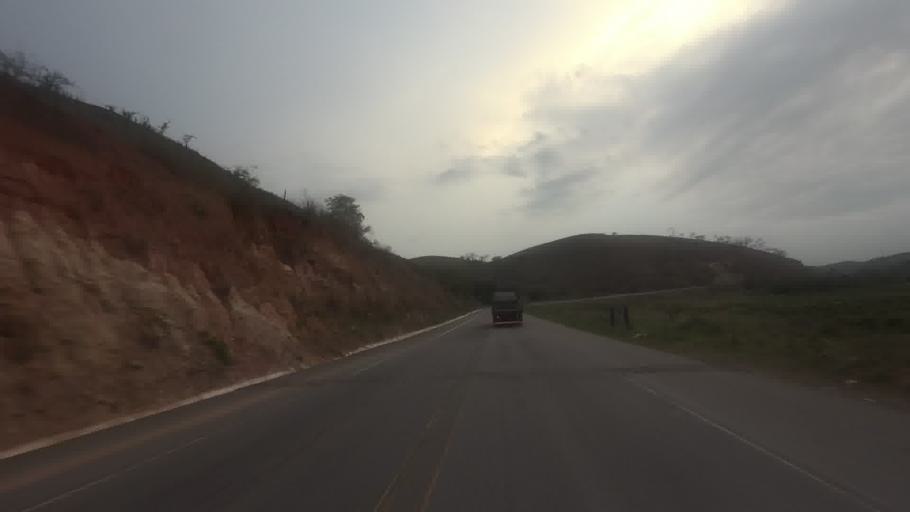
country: BR
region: Minas Gerais
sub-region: Alem Paraiba
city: Alem Paraiba
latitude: -21.8535
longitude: -42.6477
